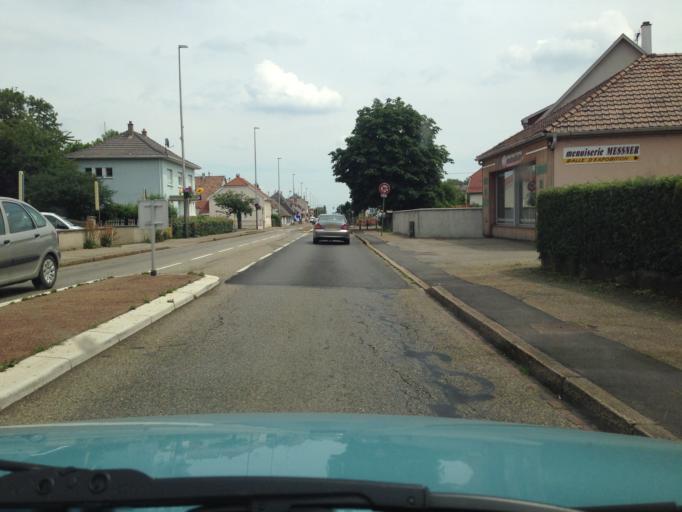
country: FR
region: Alsace
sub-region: Departement du Haut-Rhin
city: Vieux-Thann
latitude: 47.8045
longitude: 7.1205
